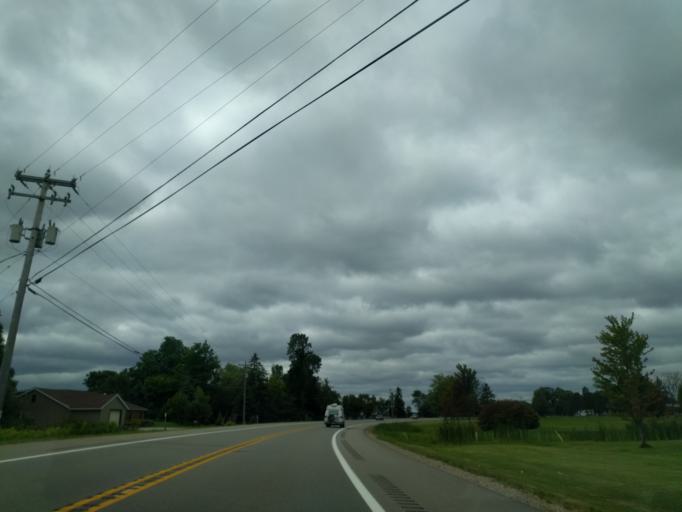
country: US
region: Michigan
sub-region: Menominee County
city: Menominee
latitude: 45.1961
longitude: -87.5391
